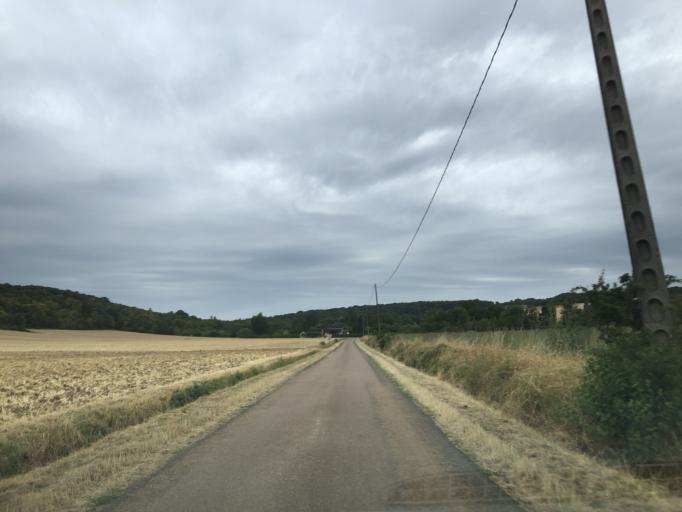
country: FR
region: Bourgogne
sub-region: Departement de l'Yonne
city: Aillant-sur-Tholon
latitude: 47.9046
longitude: 3.3331
